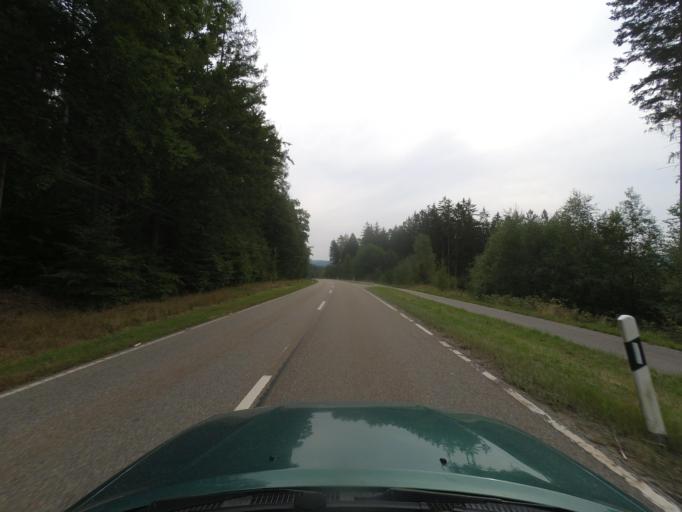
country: DE
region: Bavaria
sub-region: Upper Palatinate
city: Eslarn
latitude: 49.5829
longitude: 12.5578
